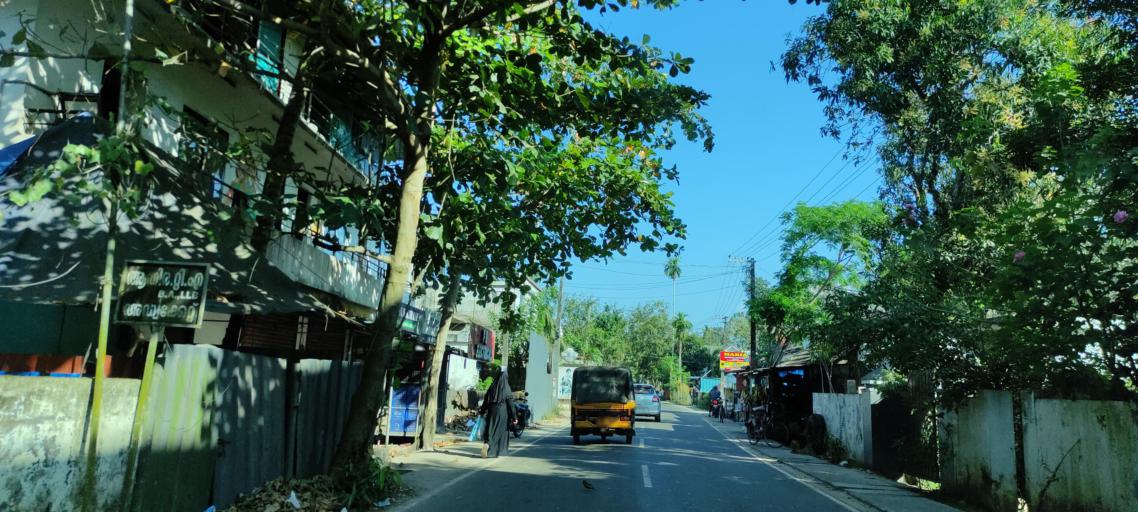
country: IN
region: Kerala
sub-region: Alappuzha
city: Shertallai
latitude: 9.6093
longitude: 76.3313
